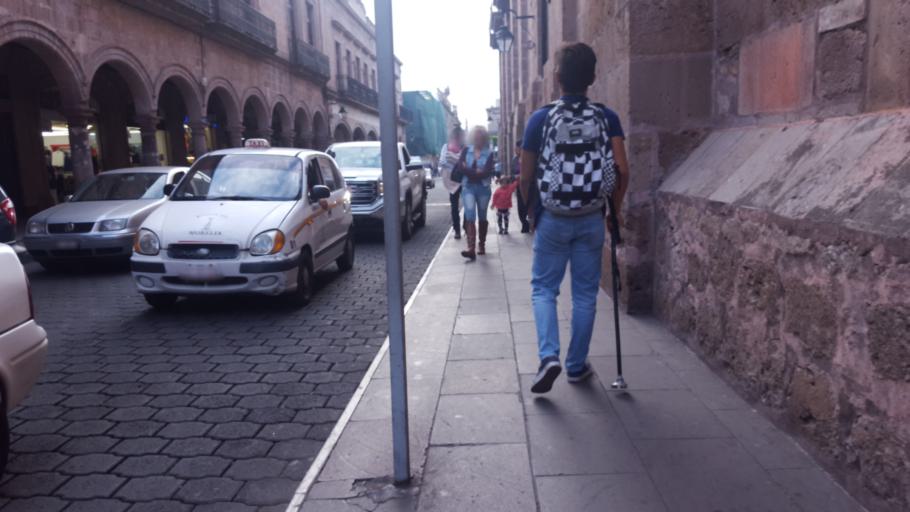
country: MX
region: Michoacan
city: Morelia
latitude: 19.7019
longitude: -101.1925
